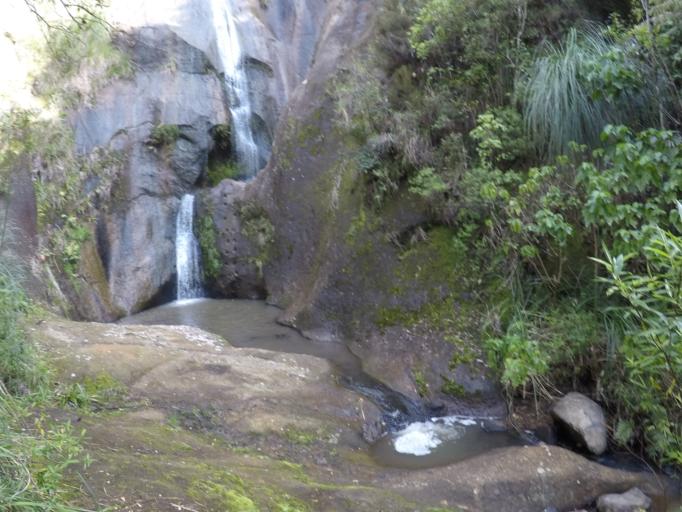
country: NZ
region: Bay of Plenty
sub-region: Western Bay of Plenty District
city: Waihi Beach
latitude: -37.3807
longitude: 175.9248
